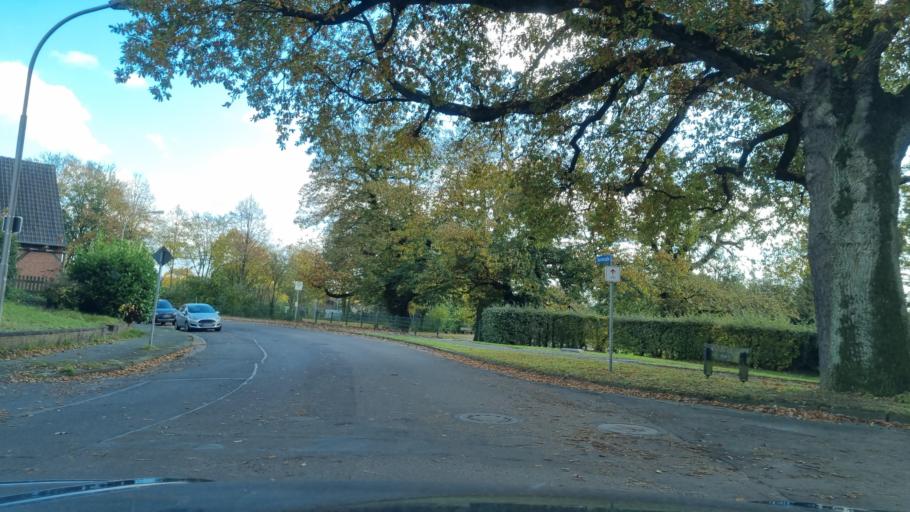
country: DE
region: North Rhine-Westphalia
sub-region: Regierungsbezirk Dusseldorf
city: Kleve
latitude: 51.7751
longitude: 6.1030
